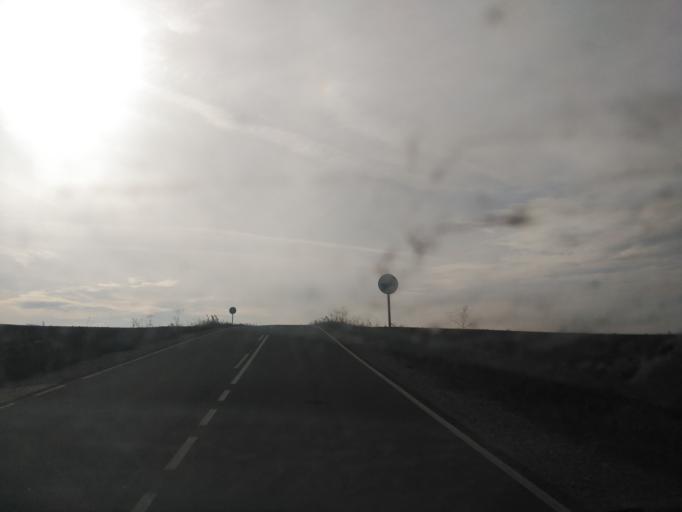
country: ES
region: Castille and Leon
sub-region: Provincia de Salamanca
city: Cabrerizos
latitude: 40.9875
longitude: -5.6011
